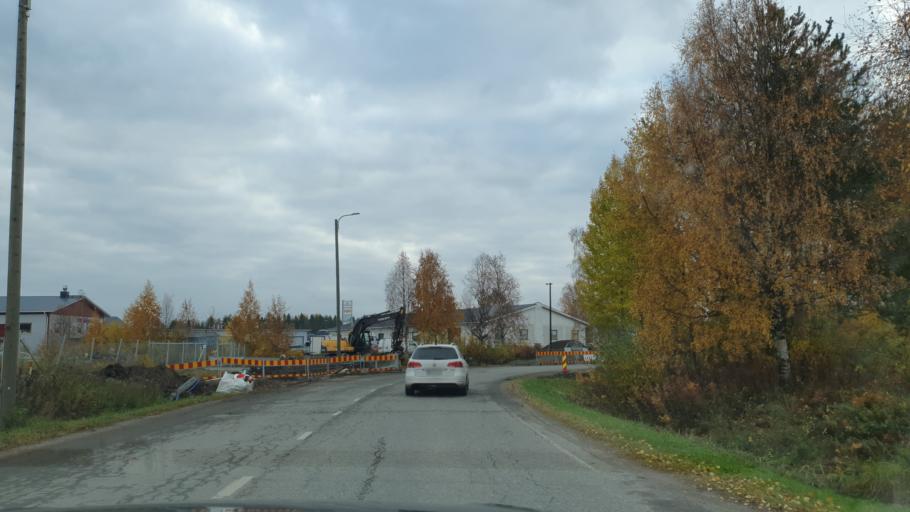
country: FI
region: Lapland
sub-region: Rovaniemi
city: Rovaniemi
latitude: 66.4918
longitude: 25.6712
